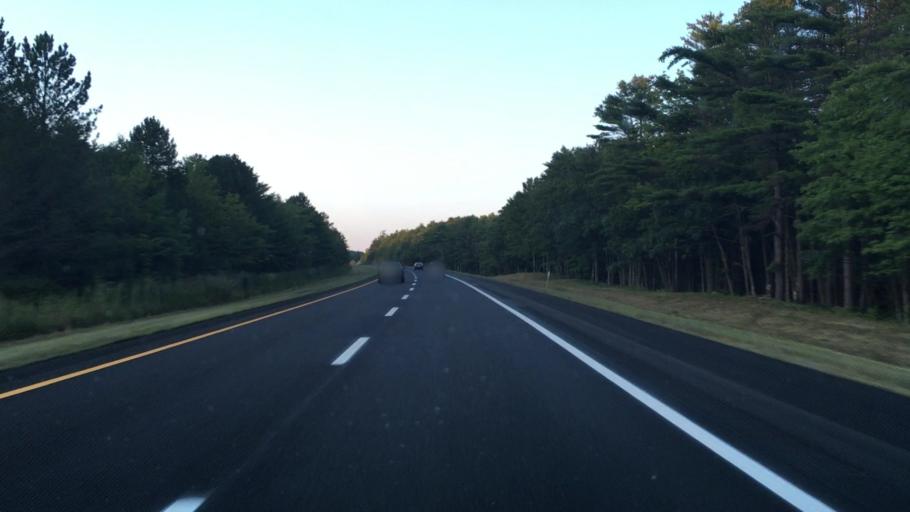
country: US
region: Maine
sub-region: Sagadahoc County
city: Topsham
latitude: 43.9844
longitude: -69.9420
